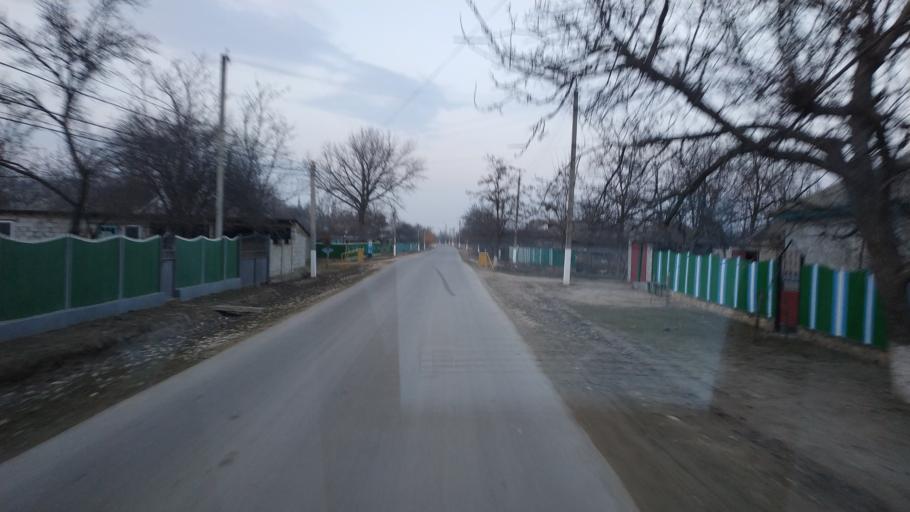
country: RO
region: Vaslui
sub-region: Comuna Stanilesti
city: Stanilesti
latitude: 46.6559
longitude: 28.3059
